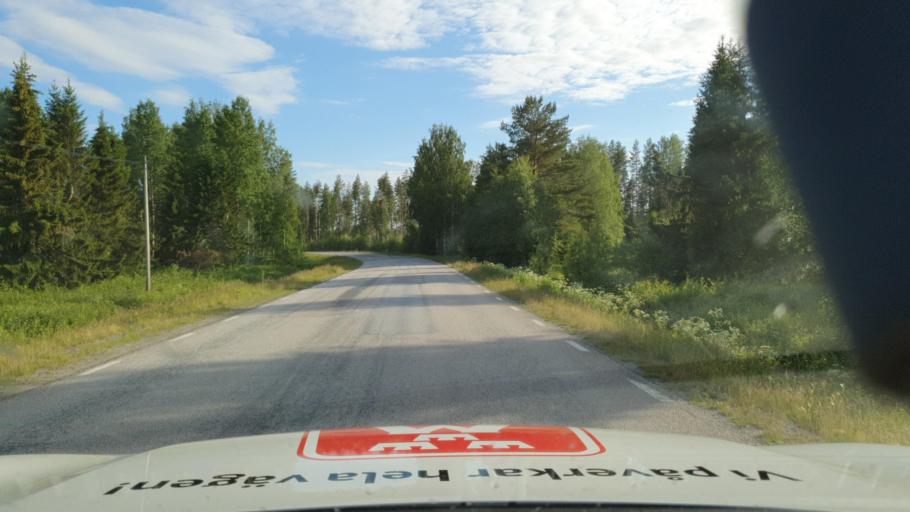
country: SE
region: Vaesterbotten
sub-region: Umea Kommun
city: Roback
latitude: 63.9288
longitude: 20.1465
